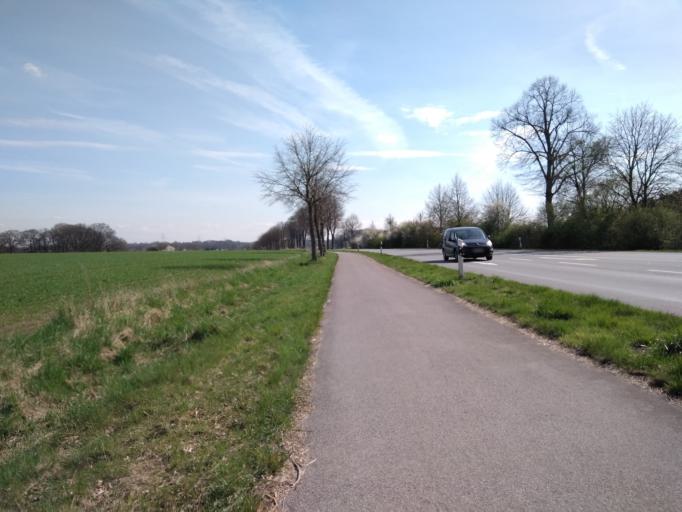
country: DE
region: North Rhine-Westphalia
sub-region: Regierungsbezirk Dusseldorf
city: Schermbeck
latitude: 51.6625
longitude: 6.8870
